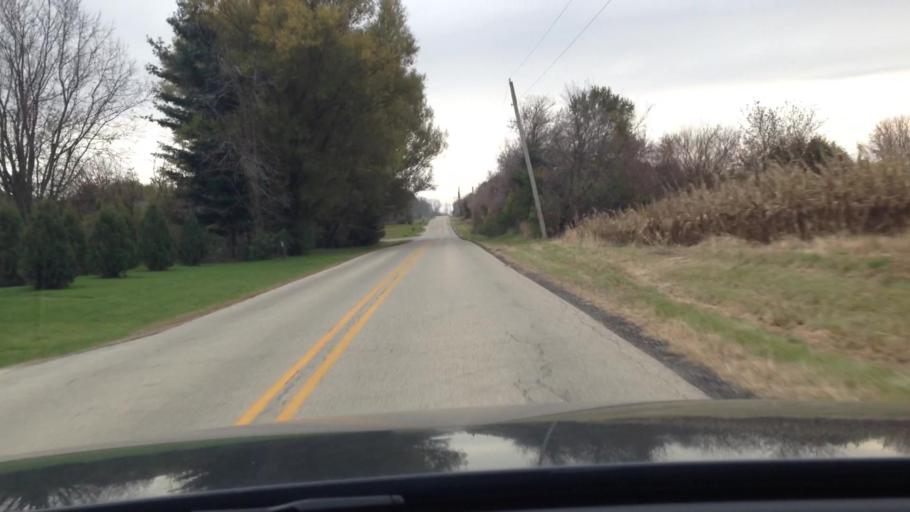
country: US
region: Illinois
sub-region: McHenry County
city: Woodstock
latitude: 42.2844
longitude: -88.4770
